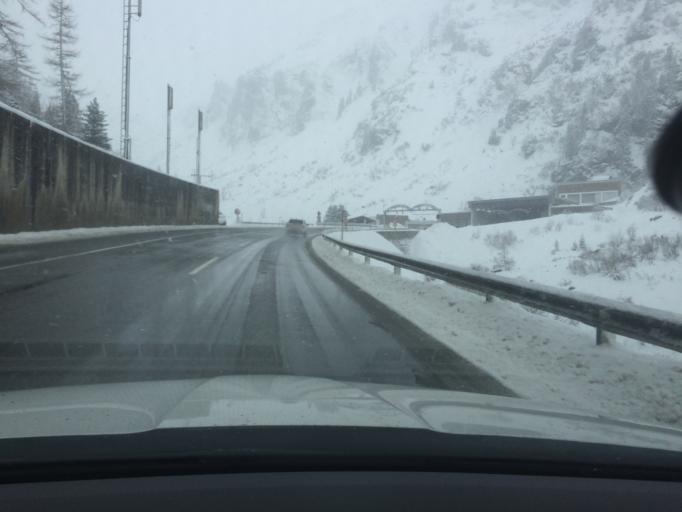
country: AT
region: Salzburg
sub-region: Politischer Bezirk Zell am See
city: Stuhlfelden
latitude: 47.1622
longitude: 12.5375
